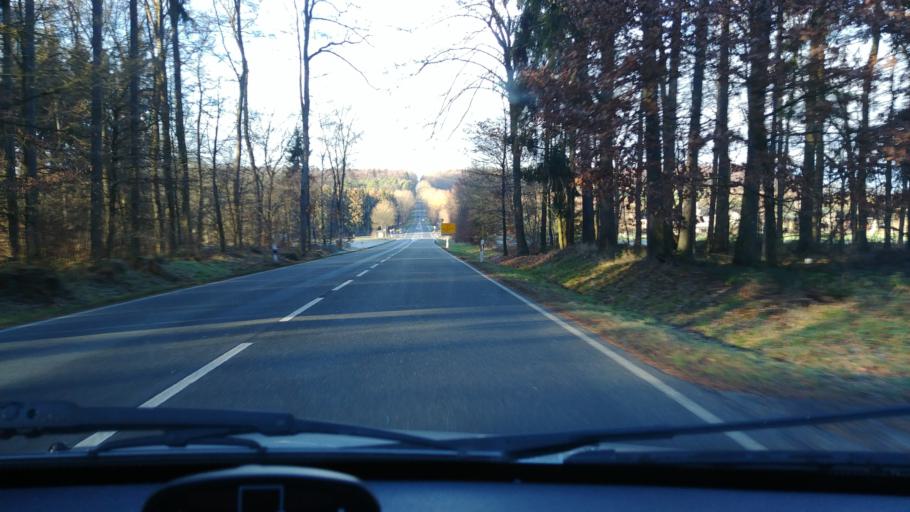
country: DE
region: Rheinland-Pfalz
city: Obertiefenbach
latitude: 50.2349
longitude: 7.8861
